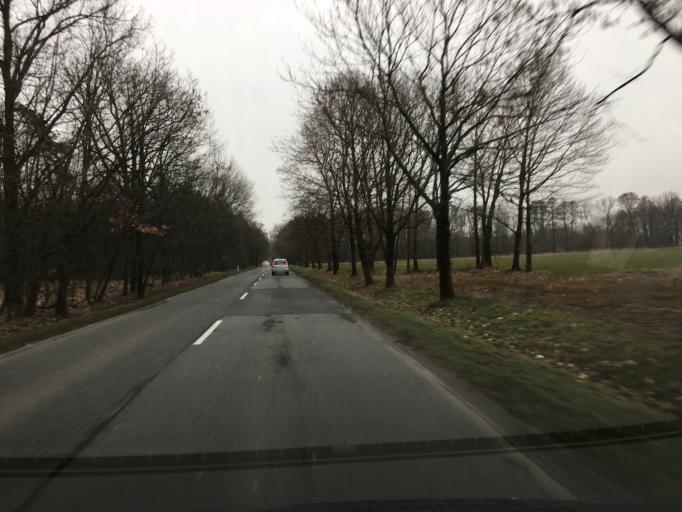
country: PL
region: Opole Voivodeship
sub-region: Powiat kedzierzynsko-kozielski
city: Bierawa
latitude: 50.3014
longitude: 18.2313
